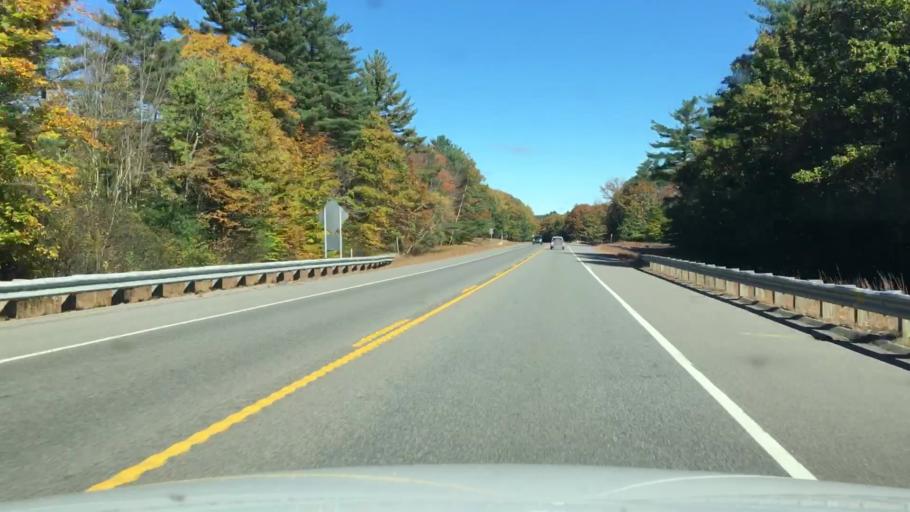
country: US
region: New Hampshire
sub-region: Carroll County
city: Sanbornville
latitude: 43.5204
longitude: -71.0274
